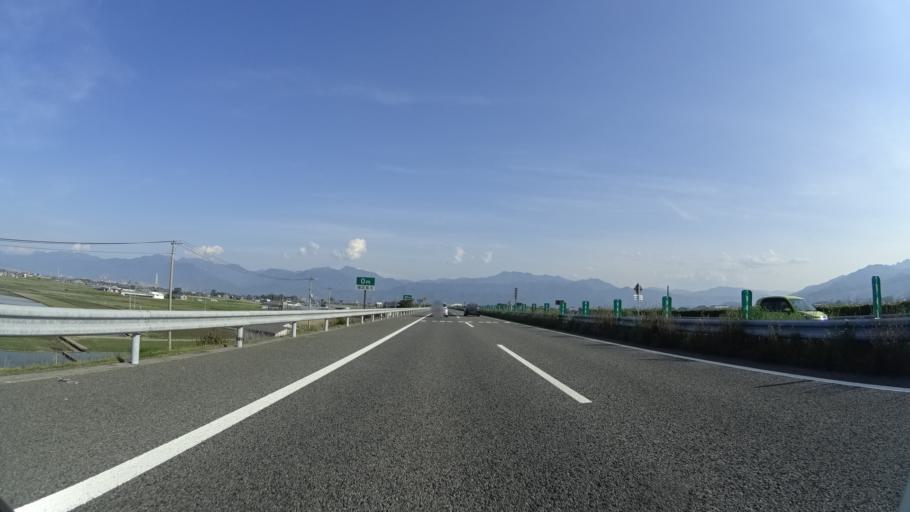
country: JP
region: Ehime
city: Saijo
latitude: 33.9594
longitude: 133.0658
